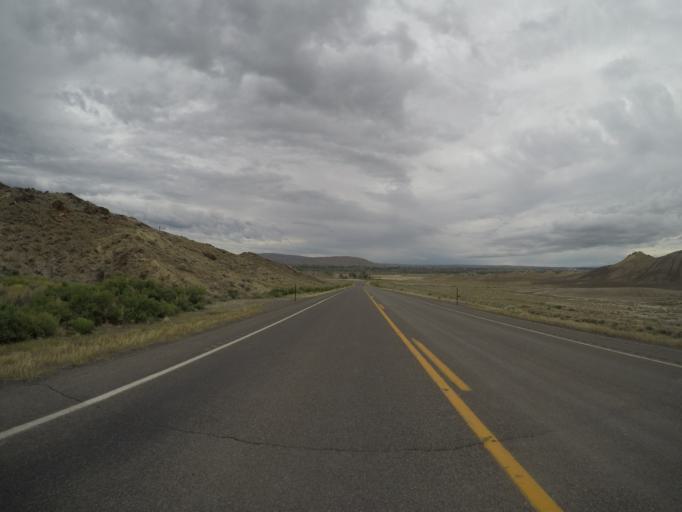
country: US
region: Wyoming
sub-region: Big Horn County
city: Lovell
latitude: 44.8846
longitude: -108.2891
